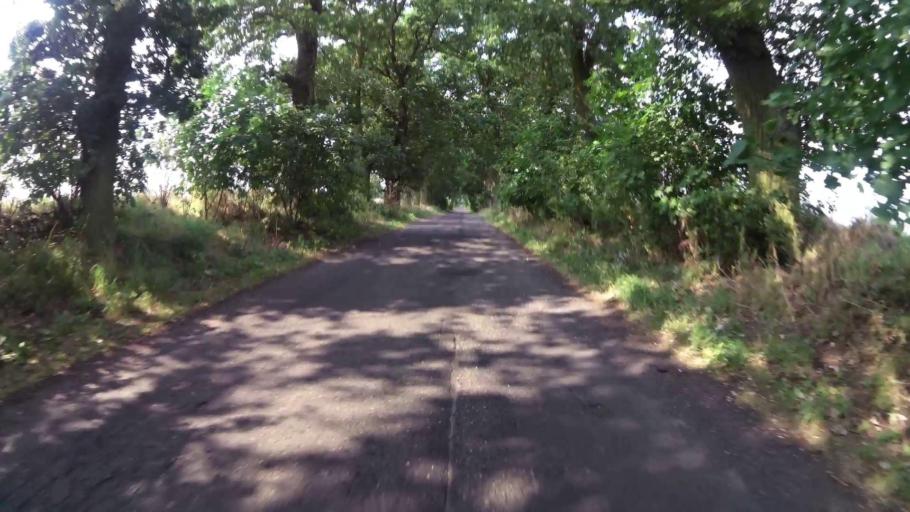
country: PL
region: West Pomeranian Voivodeship
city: Trzcinsko Zdroj
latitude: 52.9336
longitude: 14.6774
